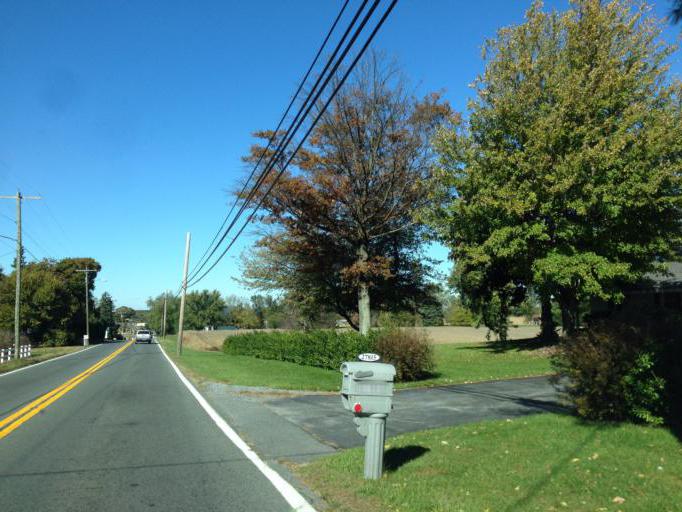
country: US
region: Maryland
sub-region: Montgomery County
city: Damascus
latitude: 39.3131
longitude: -77.1981
